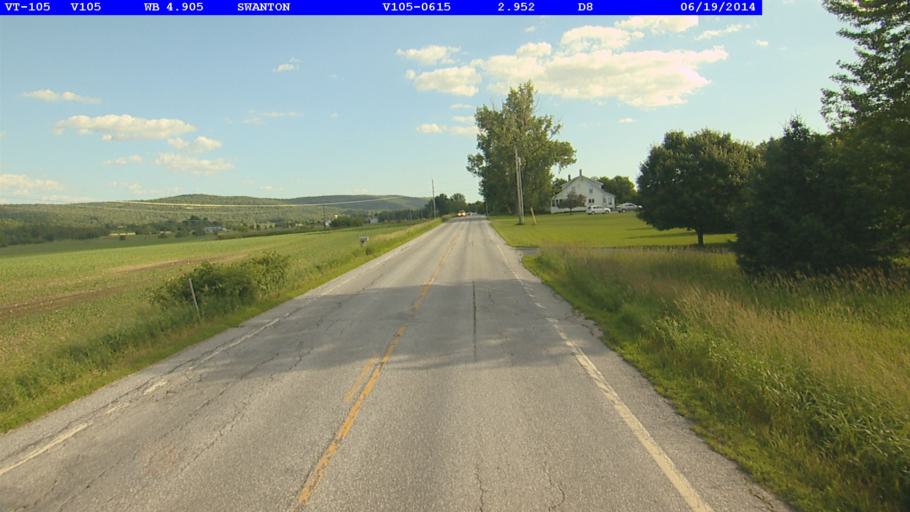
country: US
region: Vermont
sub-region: Franklin County
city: Saint Albans
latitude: 44.8749
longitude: -73.0313
